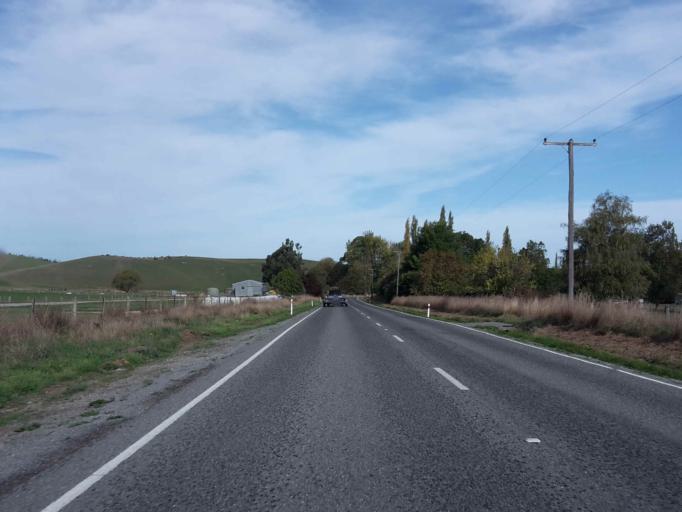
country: NZ
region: Canterbury
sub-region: Timaru District
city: Pleasant Point
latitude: -44.0679
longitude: 170.9460
